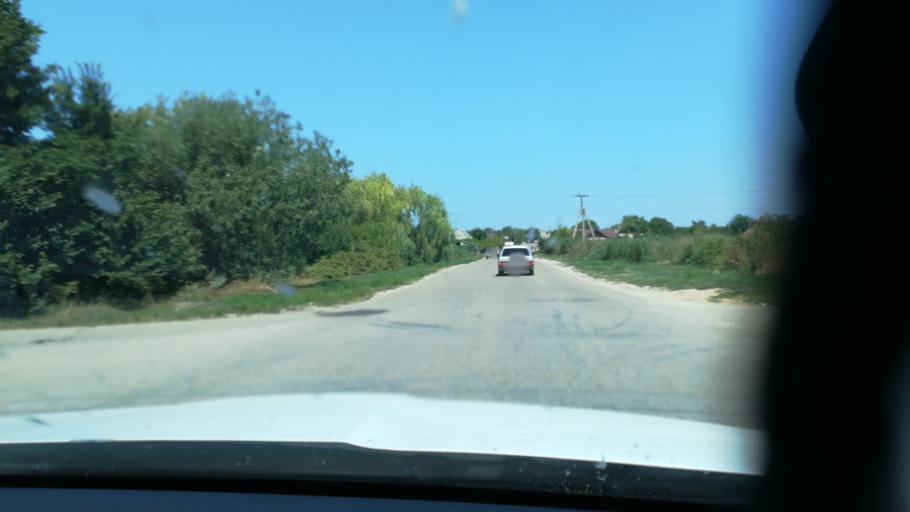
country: RU
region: Krasnodarskiy
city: Starotitarovskaya
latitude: 45.2099
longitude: 37.1453
